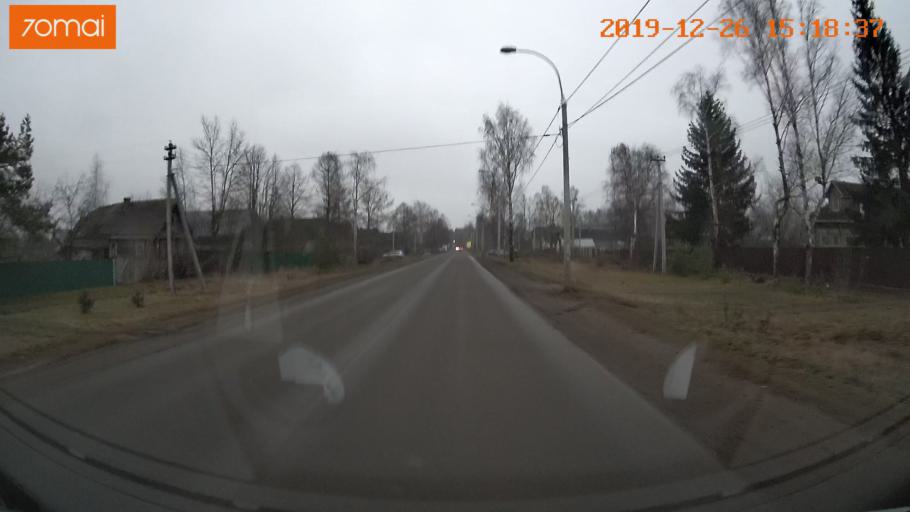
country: RU
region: Jaroslavl
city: Rybinsk
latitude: 58.0701
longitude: 38.8443
